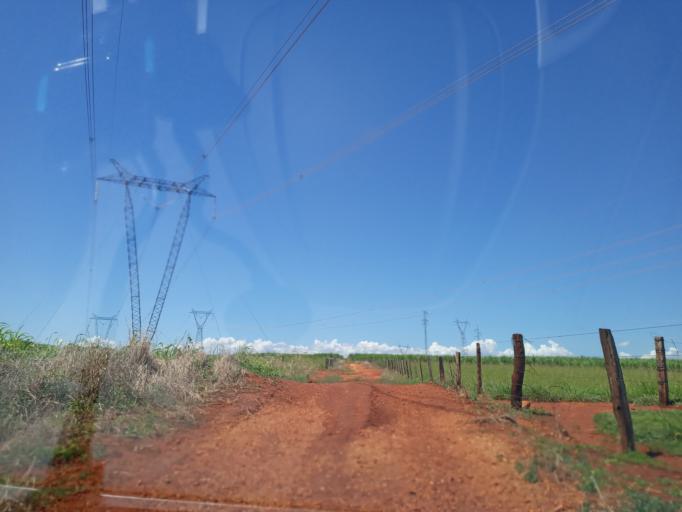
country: BR
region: Goias
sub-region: Itumbiara
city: Itumbiara
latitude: -18.3971
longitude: -49.1227
